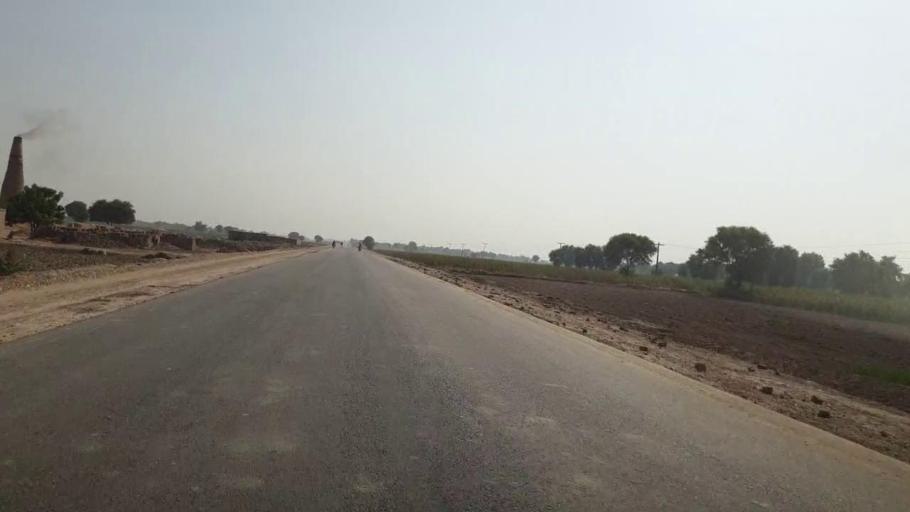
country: PK
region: Sindh
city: Dadu
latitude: 26.6608
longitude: 67.7765
